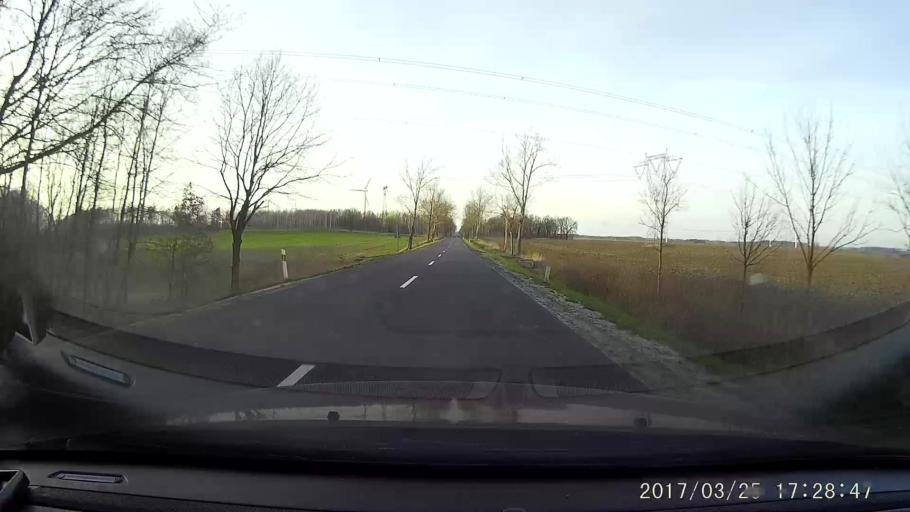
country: PL
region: Lower Silesian Voivodeship
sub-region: Powiat zgorzelecki
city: Sulikow
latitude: 51.0756
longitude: 15.0288
